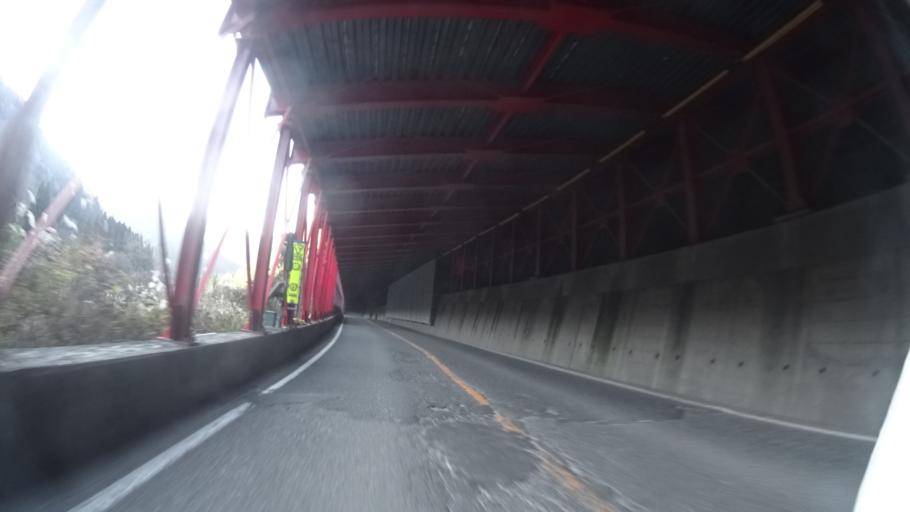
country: JP
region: Fukui
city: Ono
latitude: 35.9060
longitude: 136.6459
